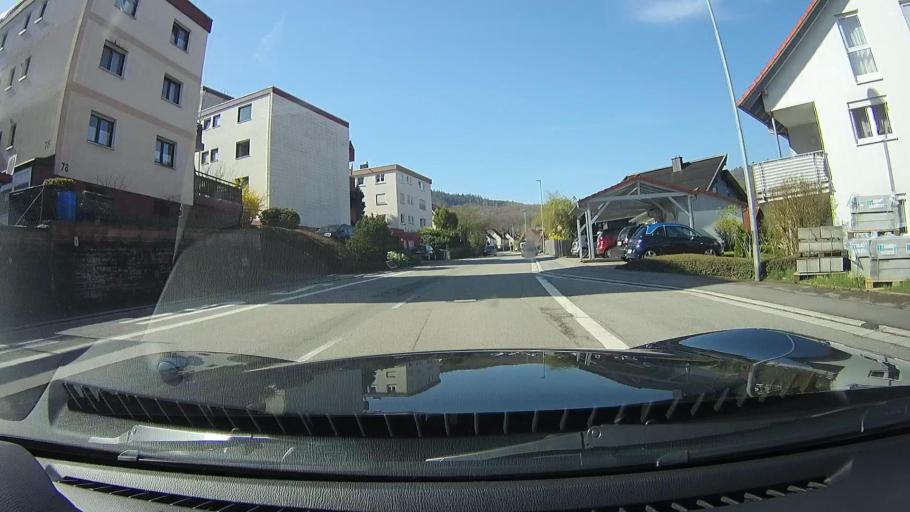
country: DE
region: Baden-Wuerttemberg
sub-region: Karlsruhe Region
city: Eberbach
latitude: 49.4523
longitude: 8.9794
